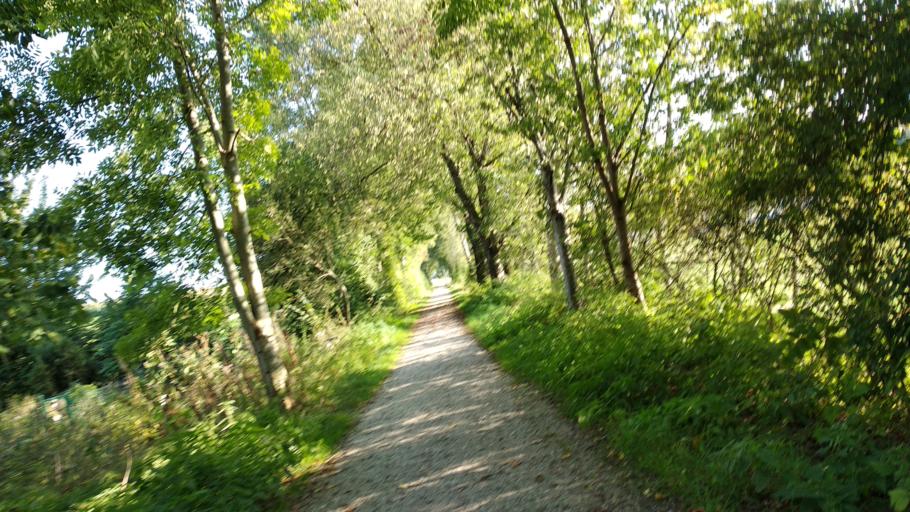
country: DE
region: Bavaria
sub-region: Upper Bavaria
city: Isen
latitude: 48.2051
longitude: 12.0651
